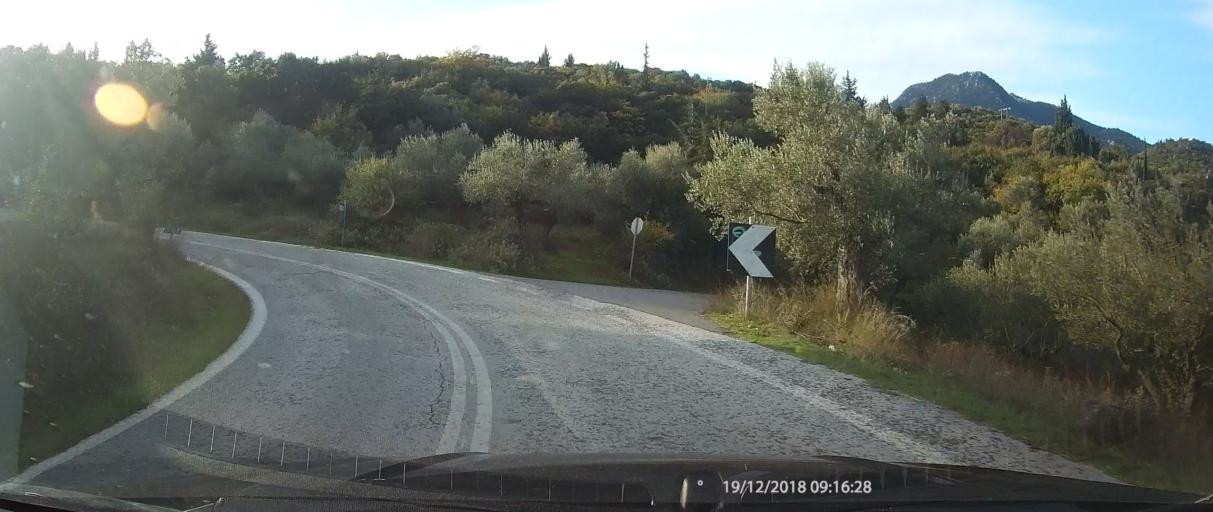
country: GR
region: Peloponnese
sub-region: Nomos Lakonias
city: Magoula
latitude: 37.0929
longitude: 22.3653
